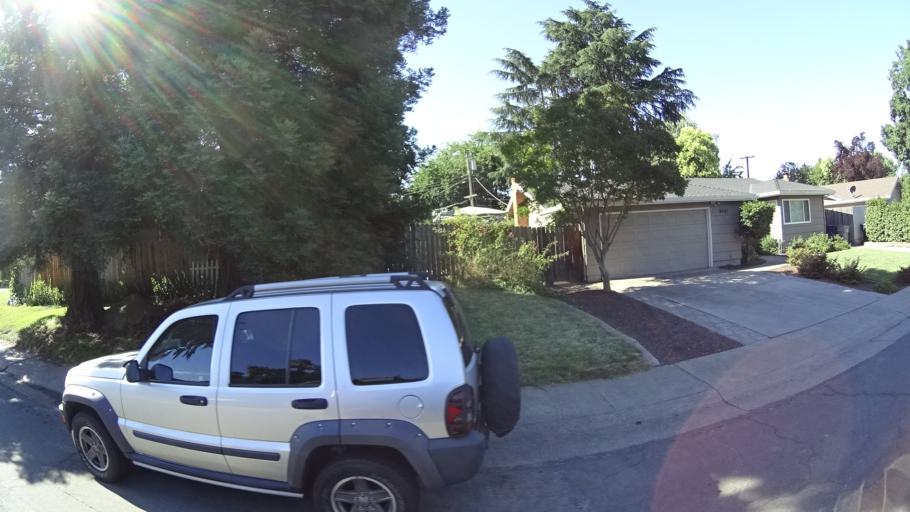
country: US
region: California
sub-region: Sacramento County
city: Rosemont
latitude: 38.5558
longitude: -121.3969
